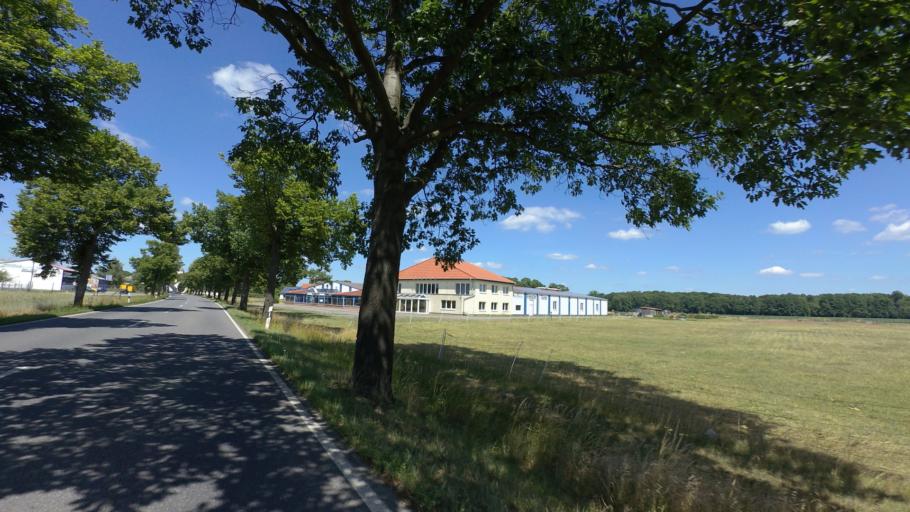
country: DE
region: Brandenburg
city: Kasel-Golzig
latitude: 51.9462
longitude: 13.6481
